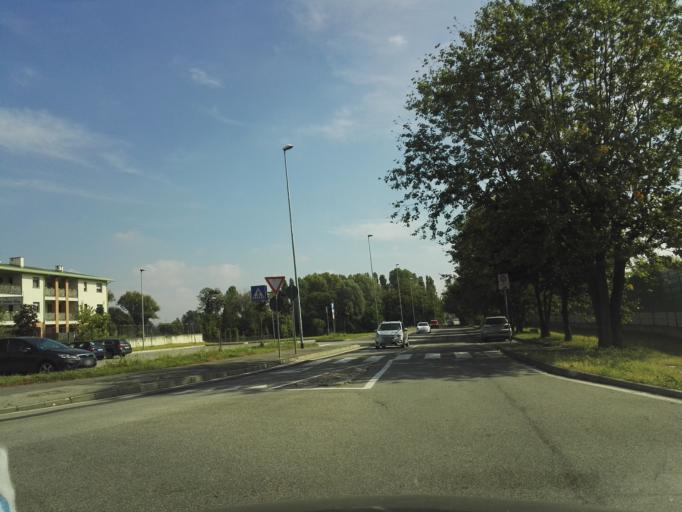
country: IT
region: Lombardy
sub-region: Citta metropolitana di Milano
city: Bettola-Zeloforomagno
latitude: 45.4279
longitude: 9.3165
